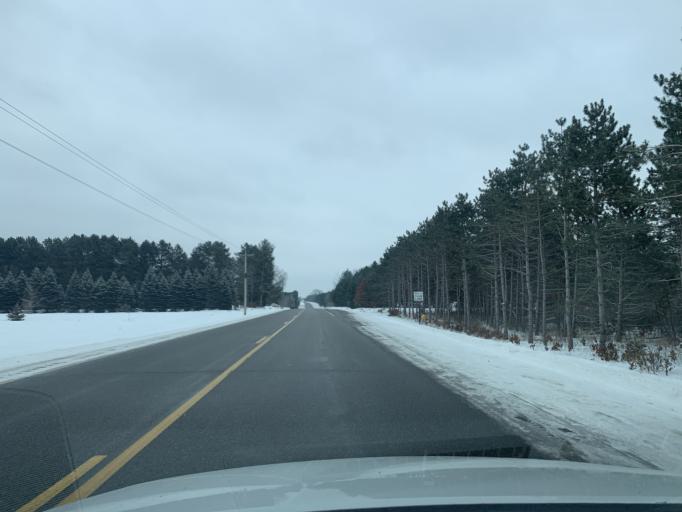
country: US
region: Minnesota
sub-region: Sherburne County
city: Zimmerman
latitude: 45.5013
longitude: -93.6205
